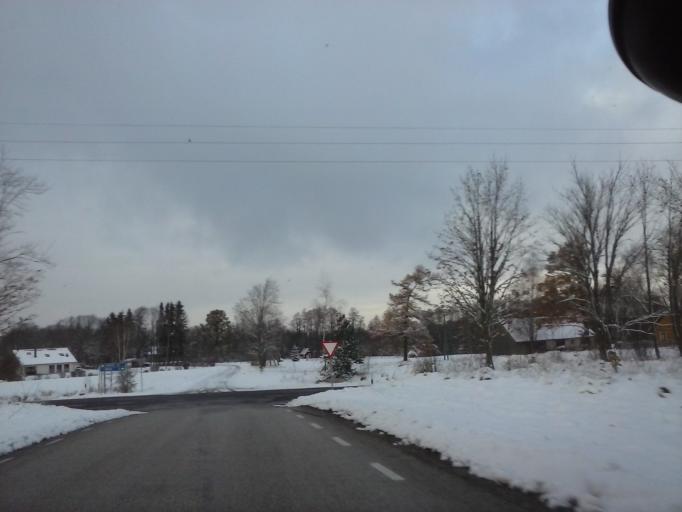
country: EE
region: Tartu
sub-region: UElenurme vald
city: Ulenurme
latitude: 58.3225
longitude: 26.8158
